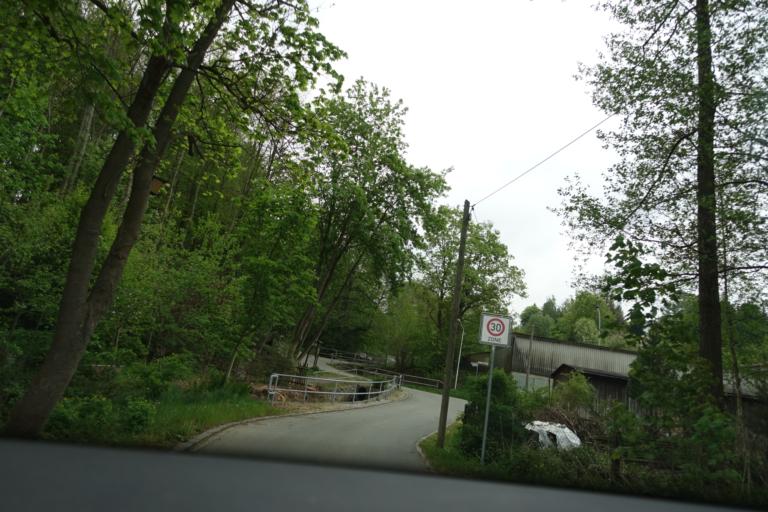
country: DE
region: Saxony
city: Eppendorf
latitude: 50.8040
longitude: 13.2189
